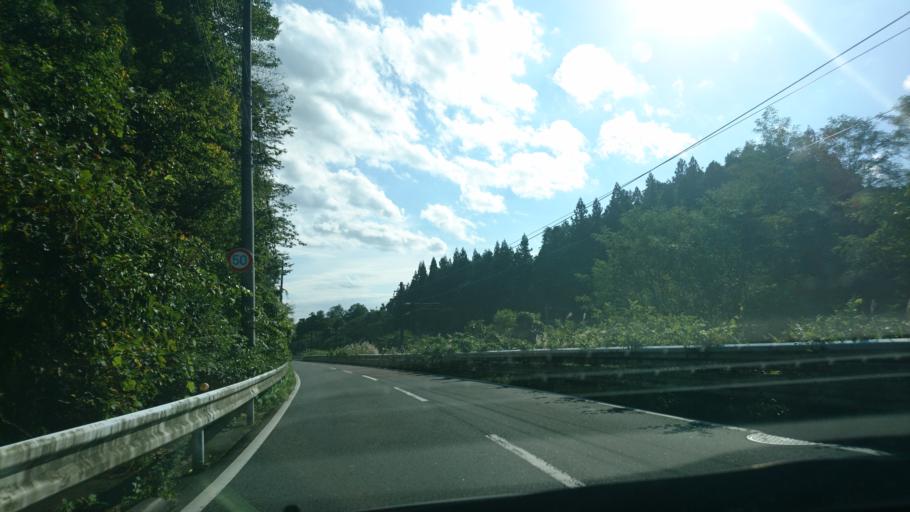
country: JP
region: Iwate
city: Ichinoseki
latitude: 38.8750
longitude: 141.1165
